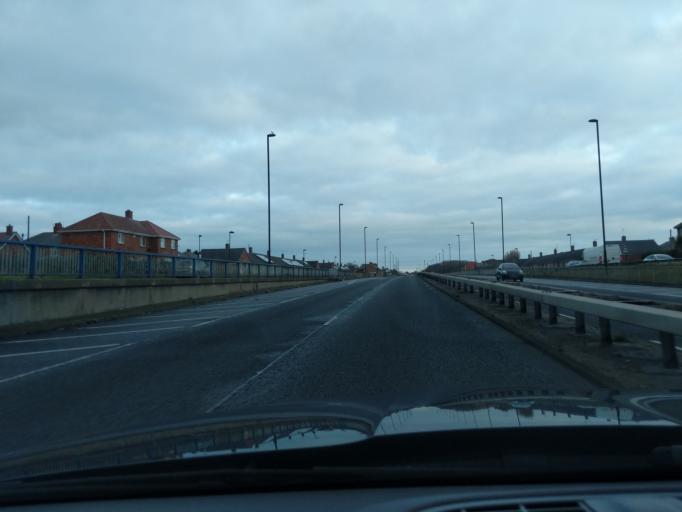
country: GB
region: England
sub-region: Borough of North Tyneside
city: Wallsend
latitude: 55.0005
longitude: -1.5413
